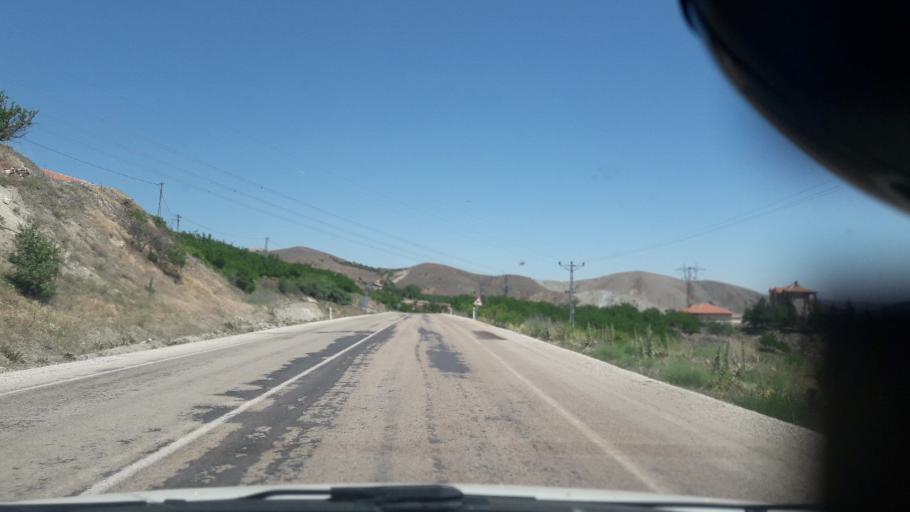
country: TR
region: Malatya
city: Hekimhan
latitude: 38.8403
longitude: 37.8364
